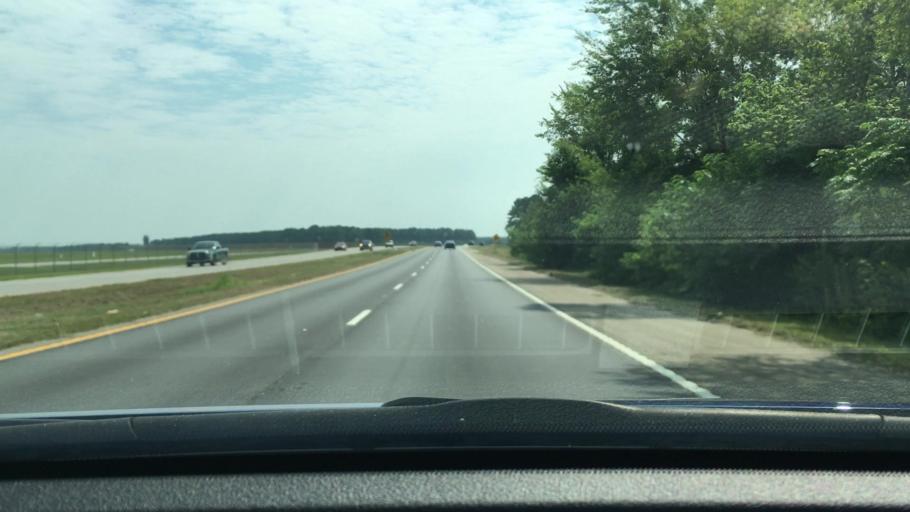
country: US
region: South Carolina
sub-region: Sumter County
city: Cherryvale
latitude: 33.9587
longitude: -80.4786
